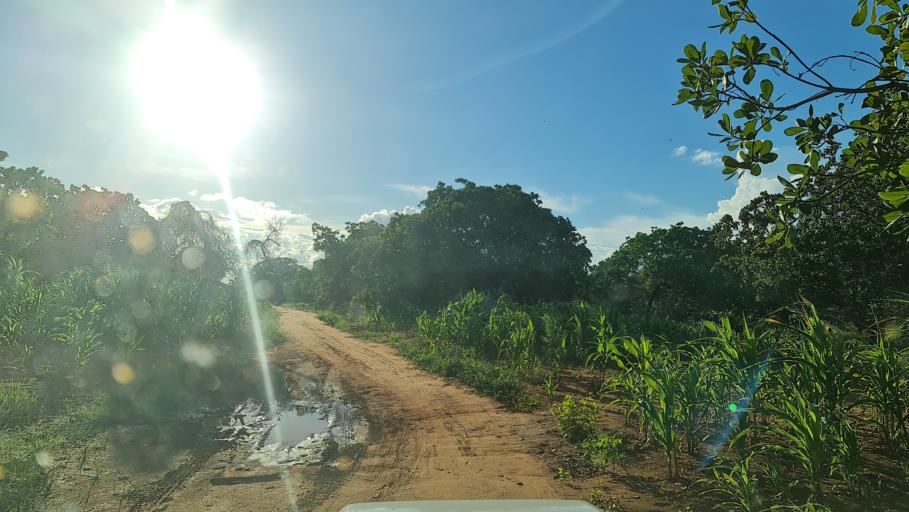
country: MZ
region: Nampula
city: Ilha de Mocambique
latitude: -14.9439
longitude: 40.1602
